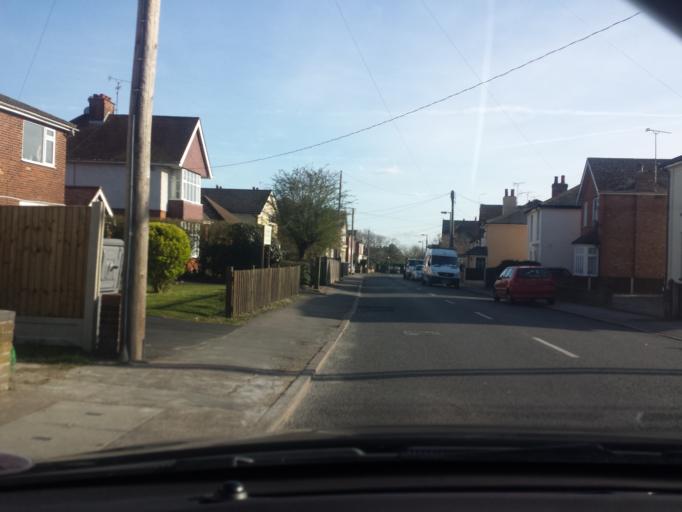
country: GB
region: England
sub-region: Essex
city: Brightlingsea
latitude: 51.8163
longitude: 1.0226
